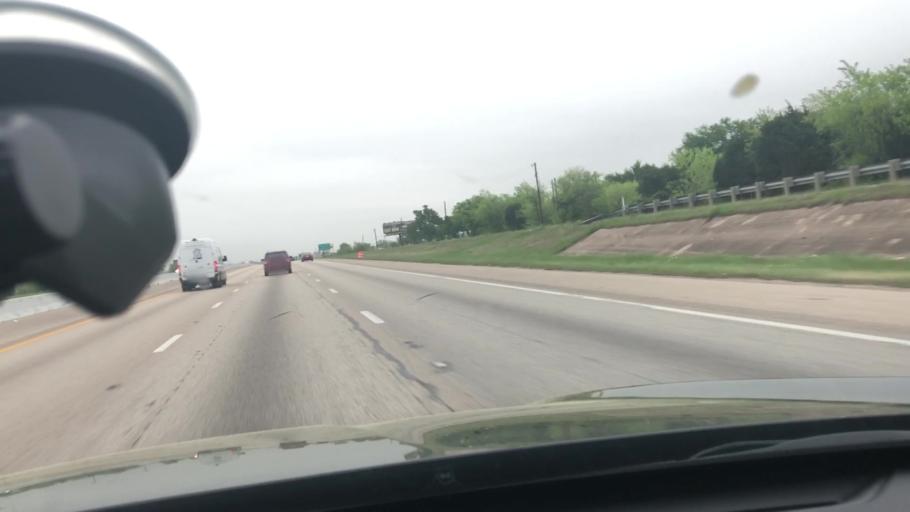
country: US
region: Texas
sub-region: Bell County
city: Belton
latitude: 31.0708
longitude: -97.4243
